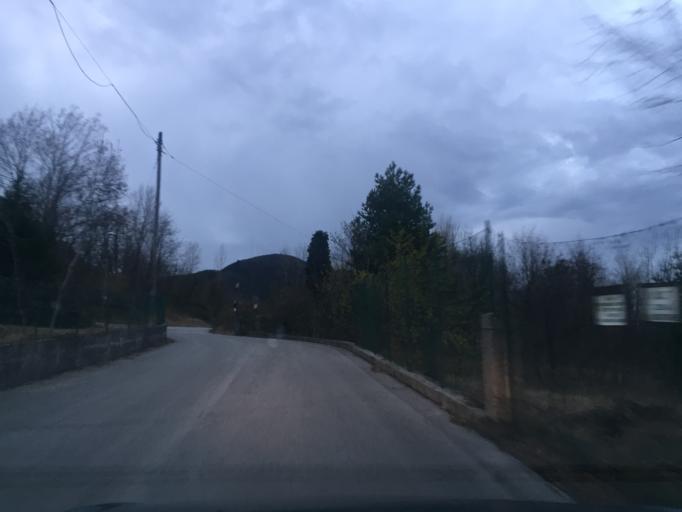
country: IT
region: Friuli Venezia Giulia
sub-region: Provincia di Udine
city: Venzone
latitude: 46.3217
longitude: 13.1387
